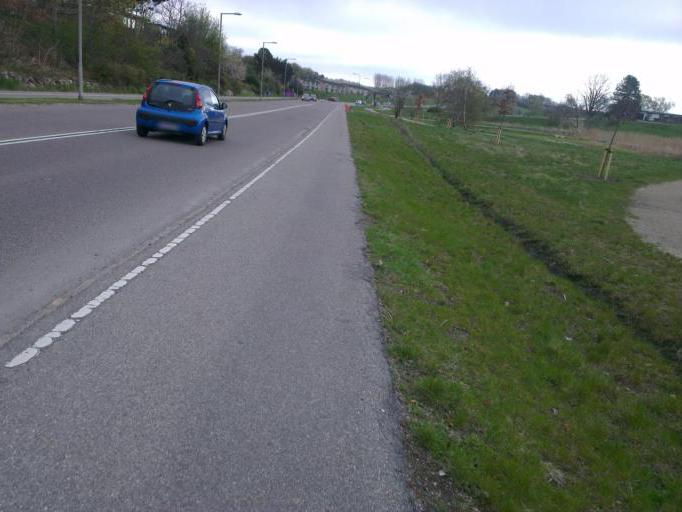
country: DK
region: Capital Region
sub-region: Frederikssund Kommune
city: Frederikssund
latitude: 55.8372
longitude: 12.0711
